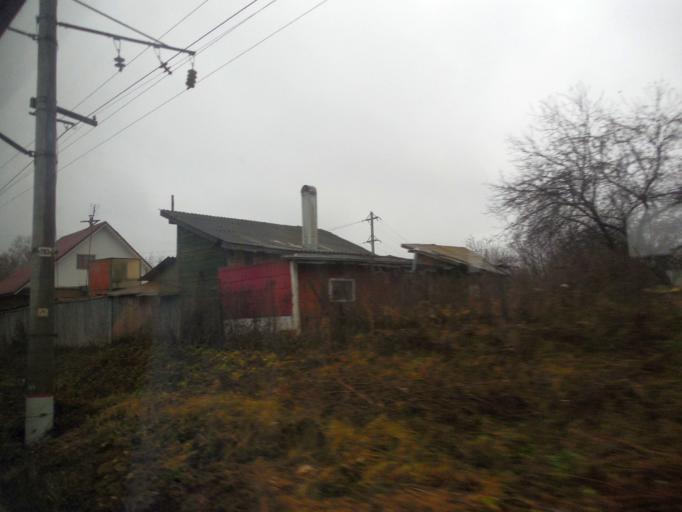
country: RU
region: Moskovskaya
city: Vostryakovo
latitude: 55.3838
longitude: 37.8135
